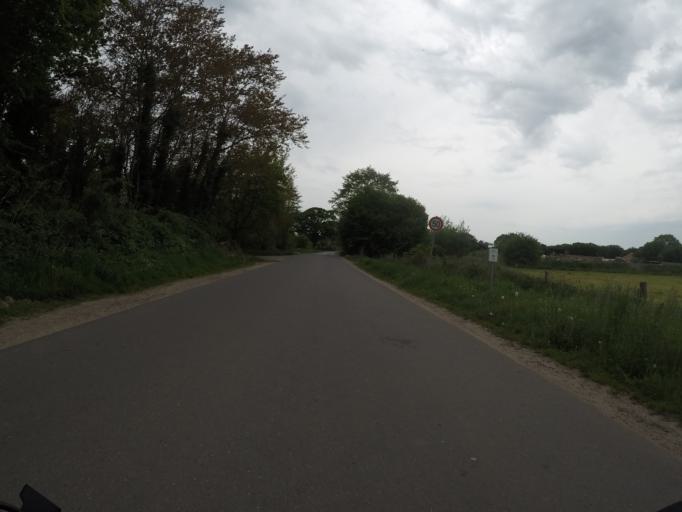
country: DE
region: Schleswig-Holstein
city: Kisdorf
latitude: 53.7829
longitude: 10.0196
